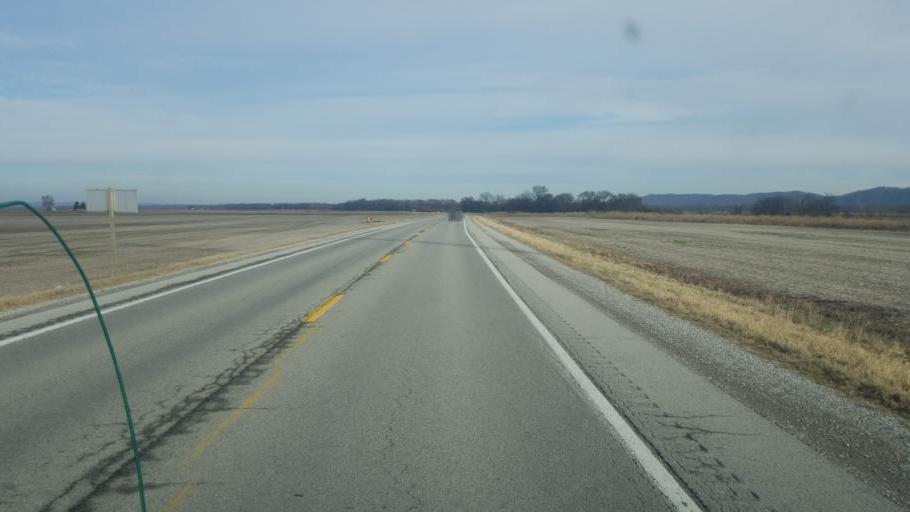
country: US
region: Missouri
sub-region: Cape Girardeau County
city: Cape Girardeau
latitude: 37.3694
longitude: -89.3938
